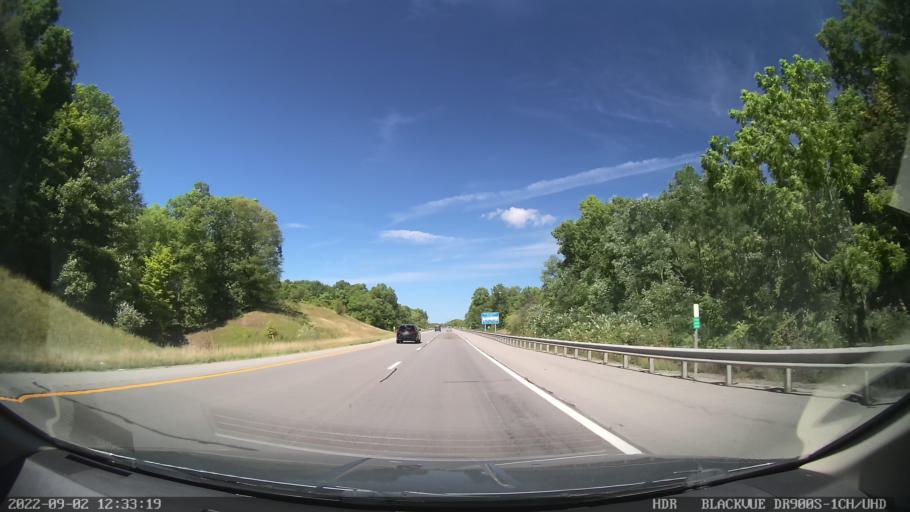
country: US
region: New York
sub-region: Livingston County
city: Dansville
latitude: 42.6360
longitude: -77.7844
